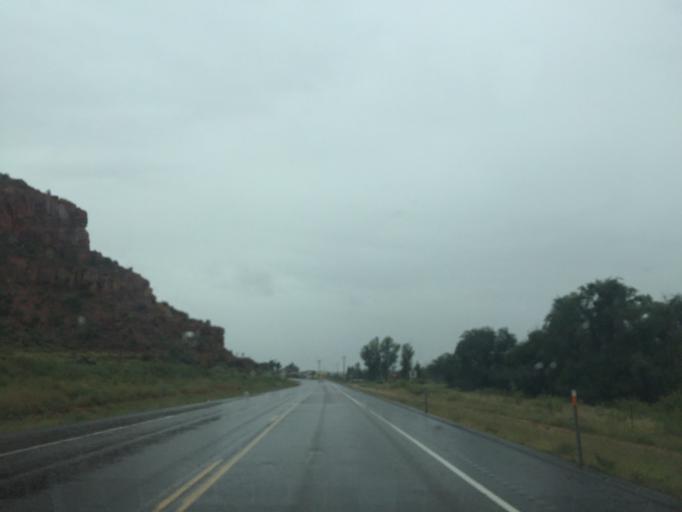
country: US
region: Utah
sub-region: Kane County
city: Kanab
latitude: 37.0623
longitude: -112.5370
